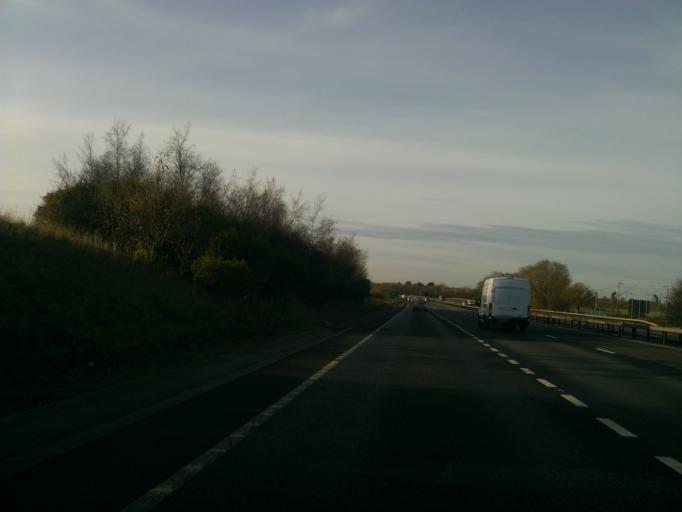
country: GB
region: England
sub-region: Essex
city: Hatfield Peverel
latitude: 51.7616
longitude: 0.5330
